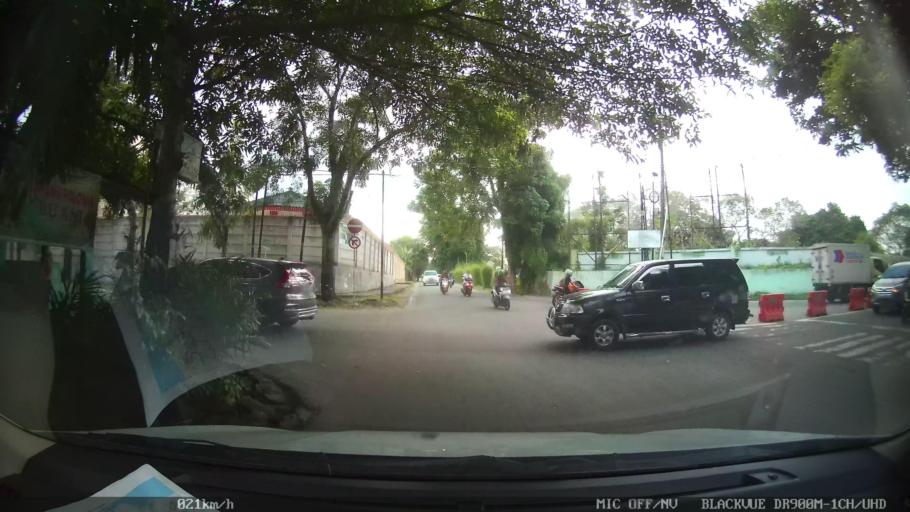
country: ID
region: North Sumatra
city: Medan
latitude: 3.5570
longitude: 98.6828
